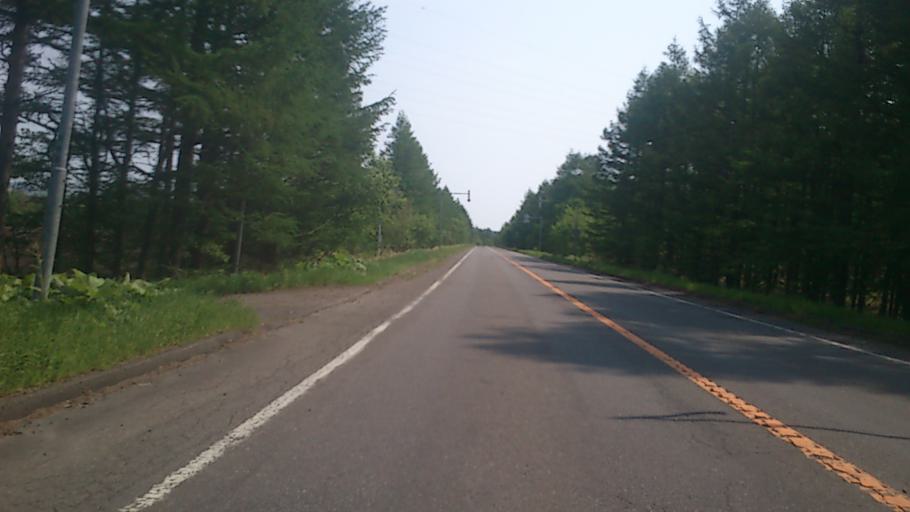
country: JP
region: Hokkaido
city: Kushiro
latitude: 43.4802
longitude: 144.5156
